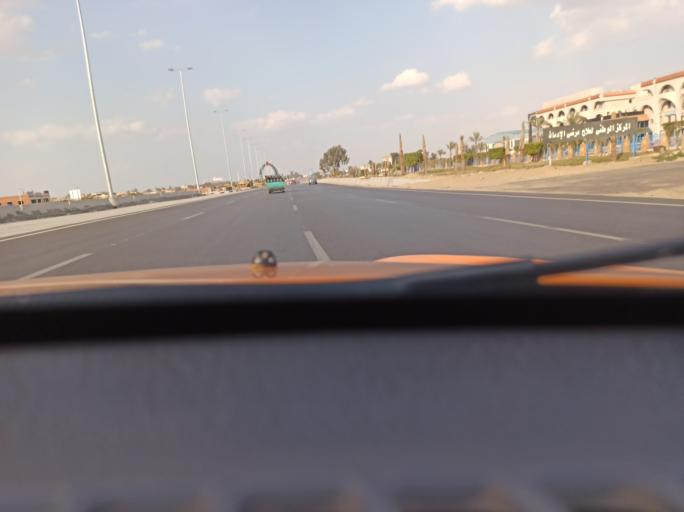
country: EG
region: Al Isma'iliyah
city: Ismailia
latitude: 30.6047
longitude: 32.2117
